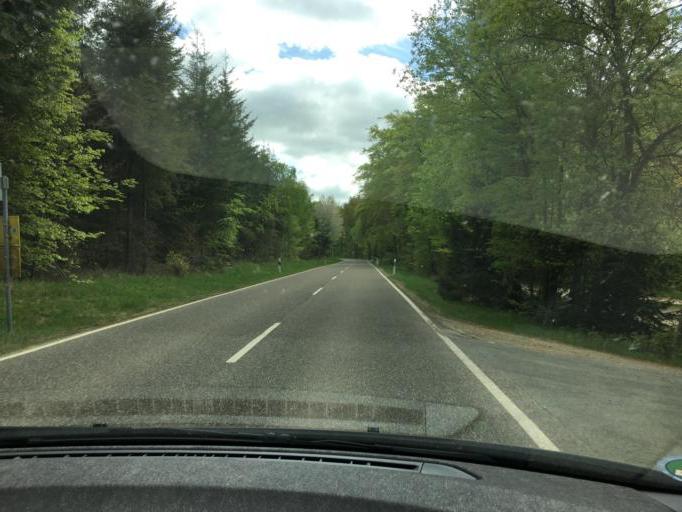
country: DE
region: North Rhine-Westphalia
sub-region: Regierungsbezirk Koln
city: Bad Munstereifel
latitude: 50.5396
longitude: 6.8223
